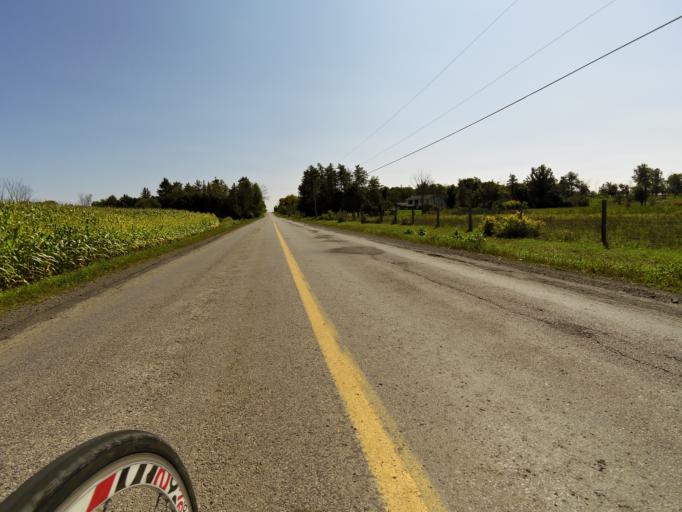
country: CA
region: Ontario
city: Bells Corners
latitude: 45.4183
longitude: -76.0407
